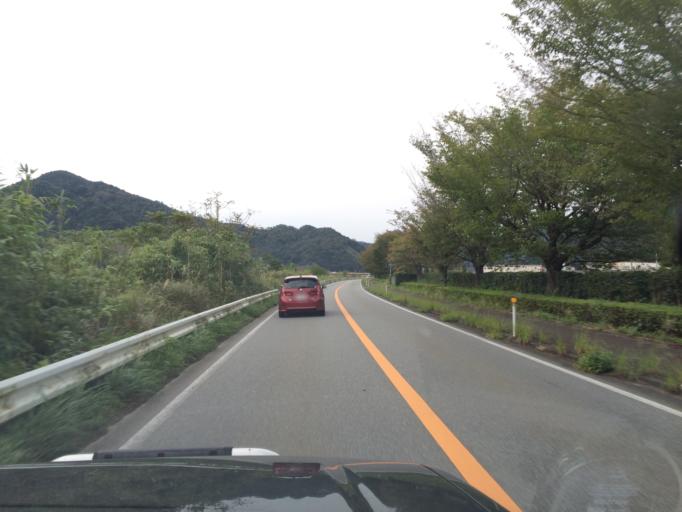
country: JP
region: Hyogo
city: Toyooka
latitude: 35.3903
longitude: 134.7995
